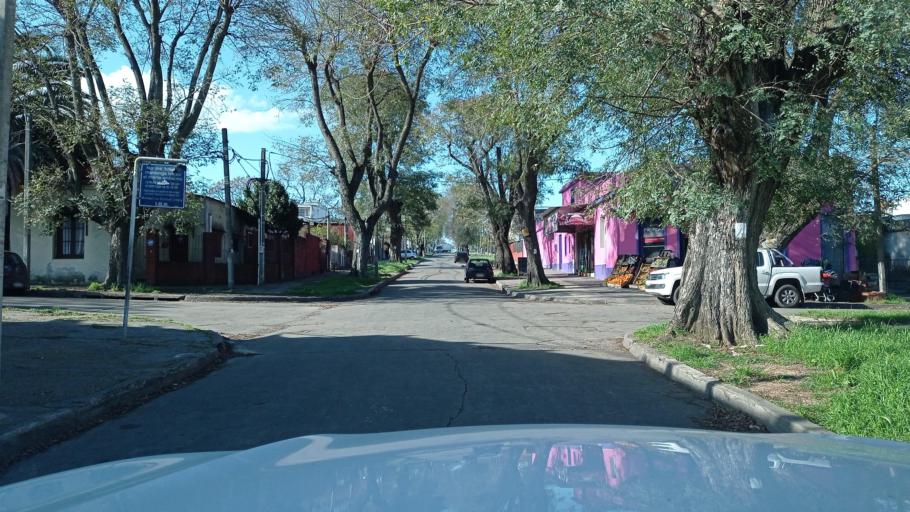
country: UY
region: Montevideo
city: Montevideo
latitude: -34.8478
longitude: -56.2099
